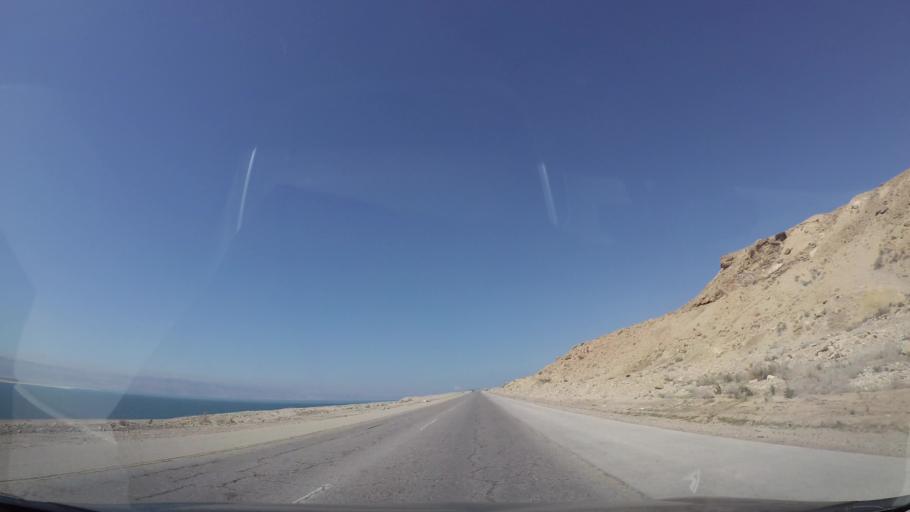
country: JO
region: Karak
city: Al Qasr
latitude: 31.3631
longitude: 35.5473
